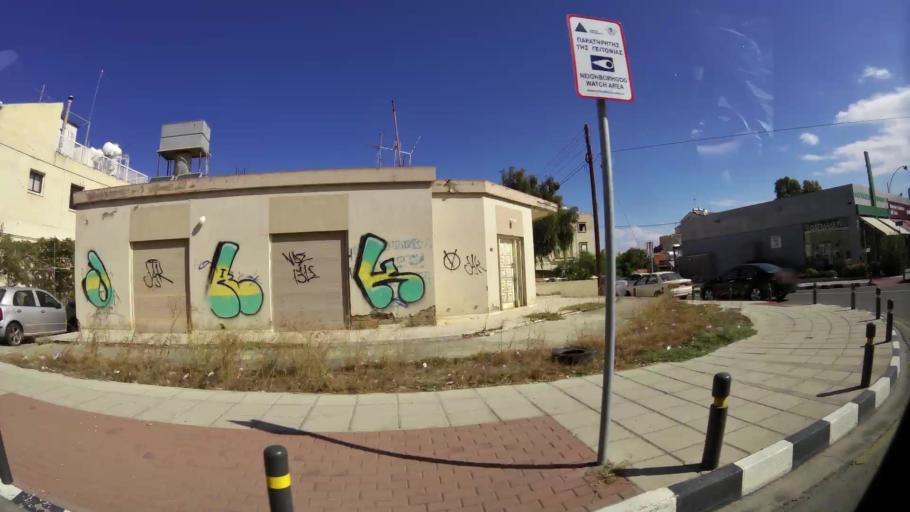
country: CY
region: Lefkosia
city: Nicosia
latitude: 35.1396
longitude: 33.3642
